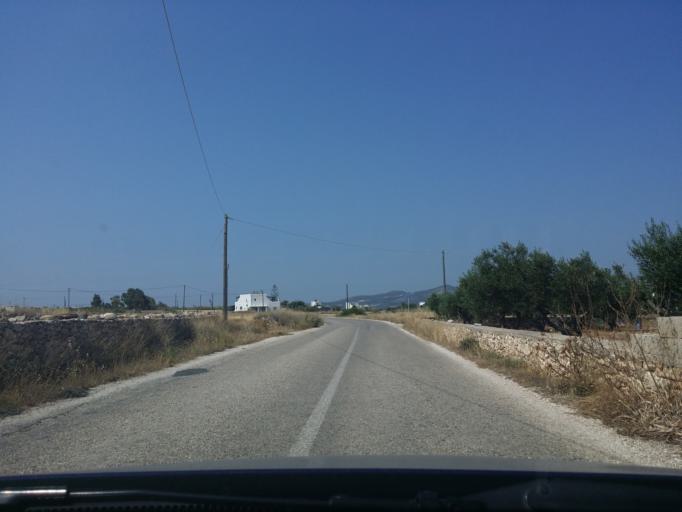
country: GR
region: South Aegean
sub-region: Nomos Kykladon
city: Antiparos
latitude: 37.0361
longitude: 25.1106
